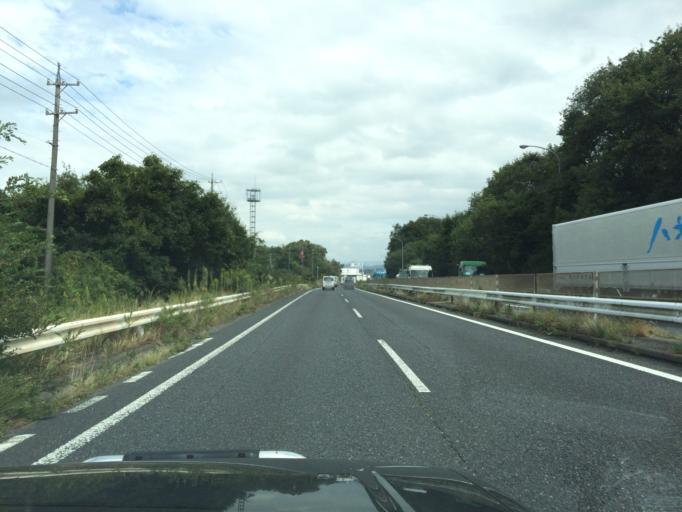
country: JP
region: Mie
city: Ueno-ebisumachi
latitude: 34.7327
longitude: 136.0998
